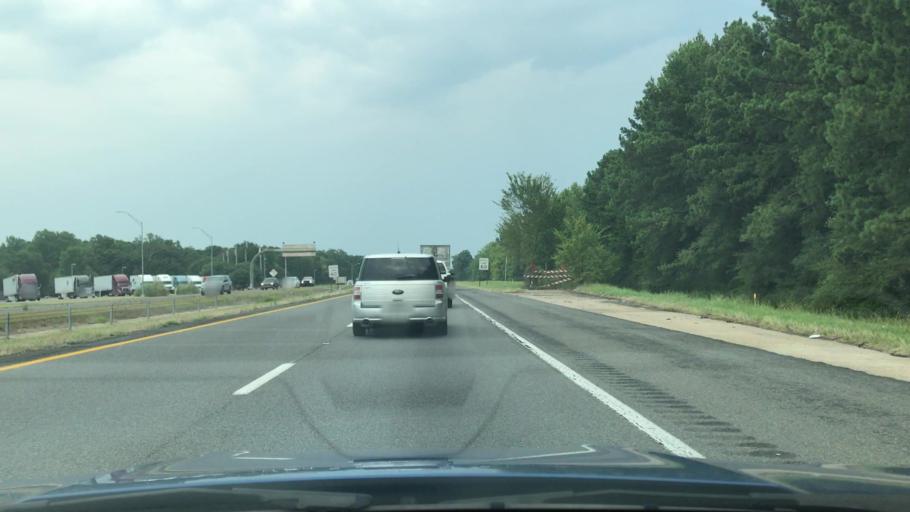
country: US
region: Texas
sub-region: Harrison County
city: Waskom
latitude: 32.4634
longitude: -94.0477
